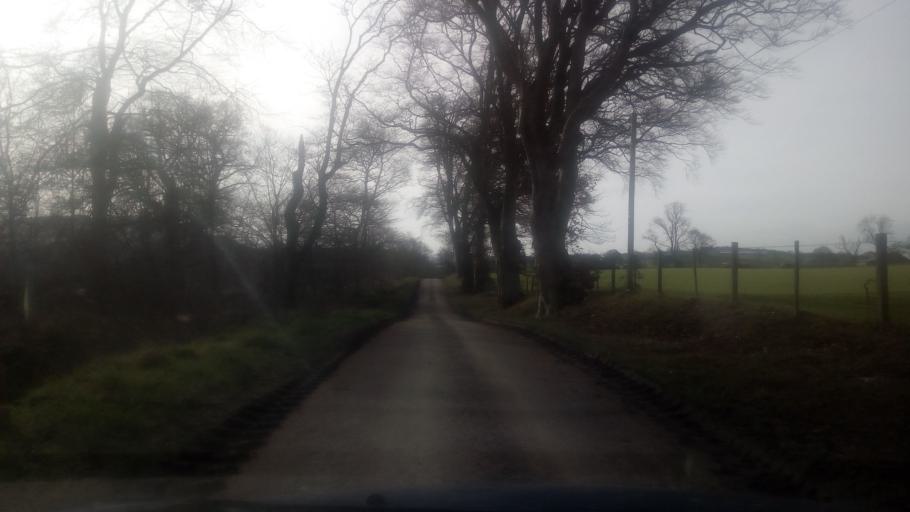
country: GB
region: Scotland
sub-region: The Scottish Borders
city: Jedburgh
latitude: 55.4225
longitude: -2.6433
